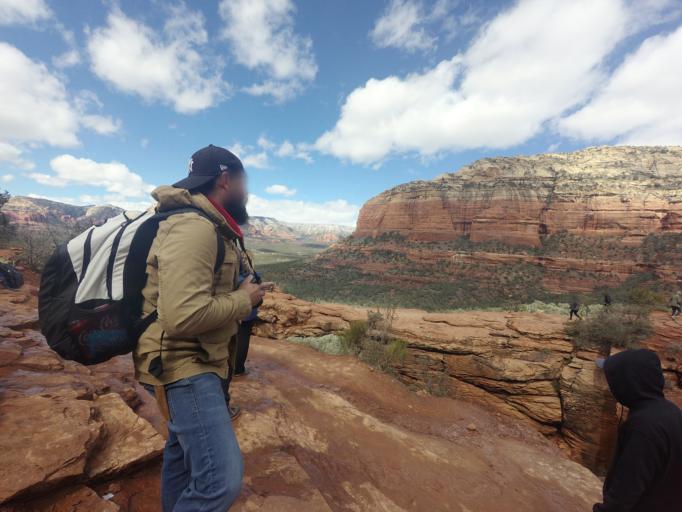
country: US
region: Arizona
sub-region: Yavapai County
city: West Sedona
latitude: 34.8974
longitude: -111.8077
